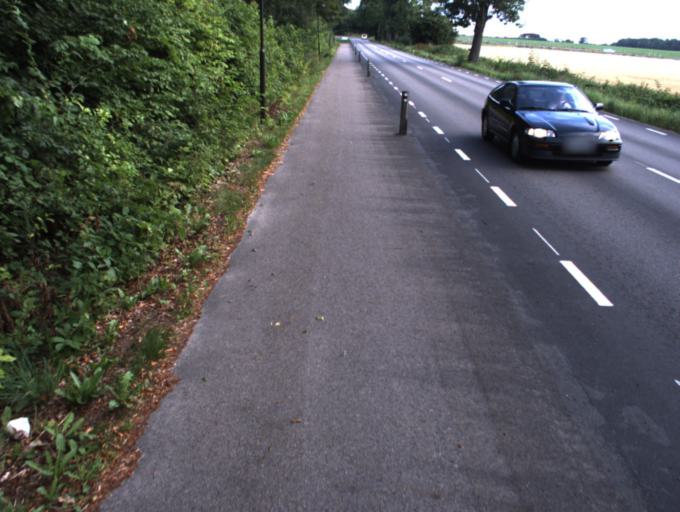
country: DK
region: Capital Region
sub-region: Helsingor Kommune
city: Helsingor
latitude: 56.1085
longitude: 12.6381
